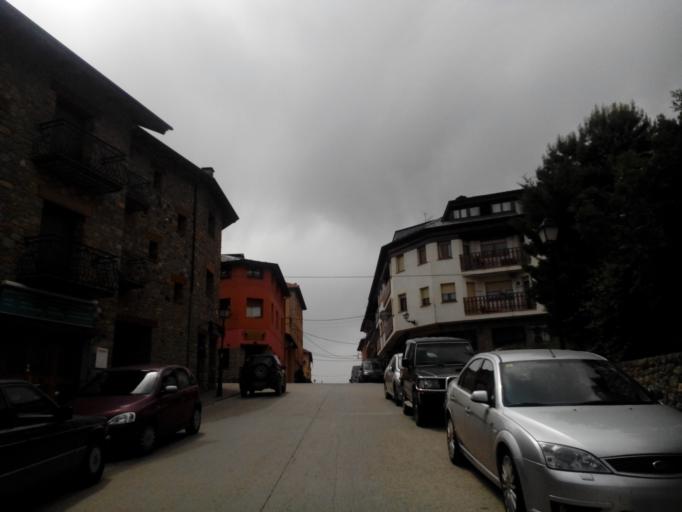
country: ES
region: Catalonia
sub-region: Provincia de Lleida
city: Bellver de Cerdanya
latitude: 42.3693
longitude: 1.7765
